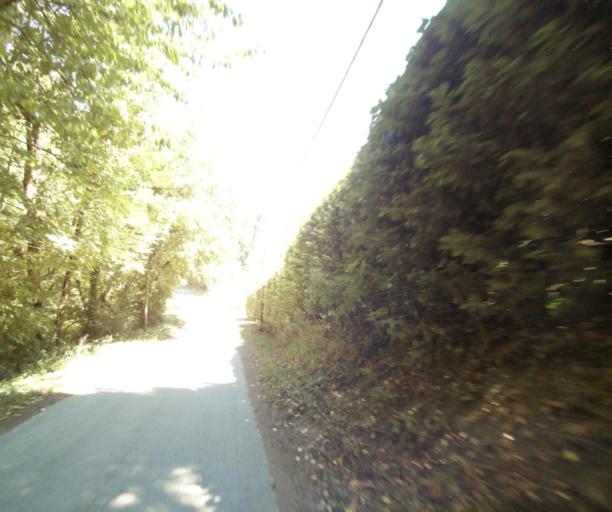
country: FR
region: Midi-Pyrenees
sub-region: Departement de la Haute-Garonne
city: Castanet-Tolosan
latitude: 43.5077
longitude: 1.4944
